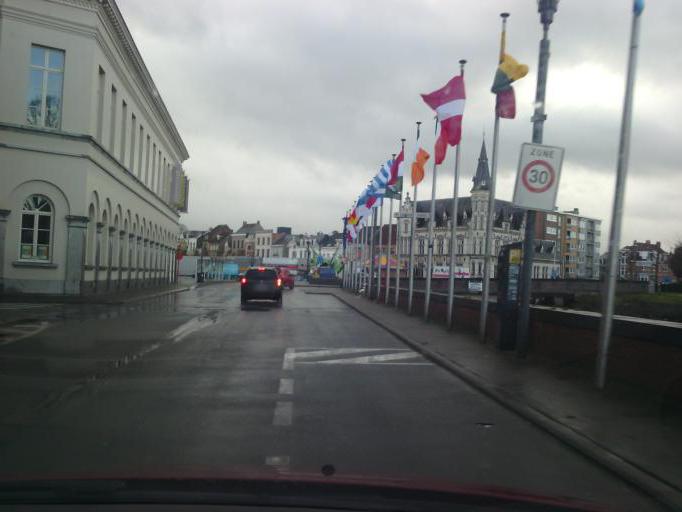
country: BE
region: Flanders
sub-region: Provincie Oost-Vlaanderen
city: Lokeren
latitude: 51.1061
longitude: 3.9900
